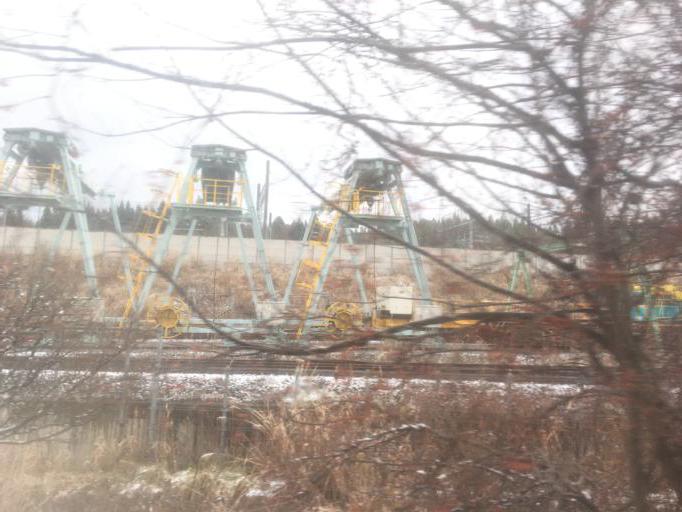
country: JP
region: Aomori
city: Goshogawara
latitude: 41.1426
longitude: 140.5167
